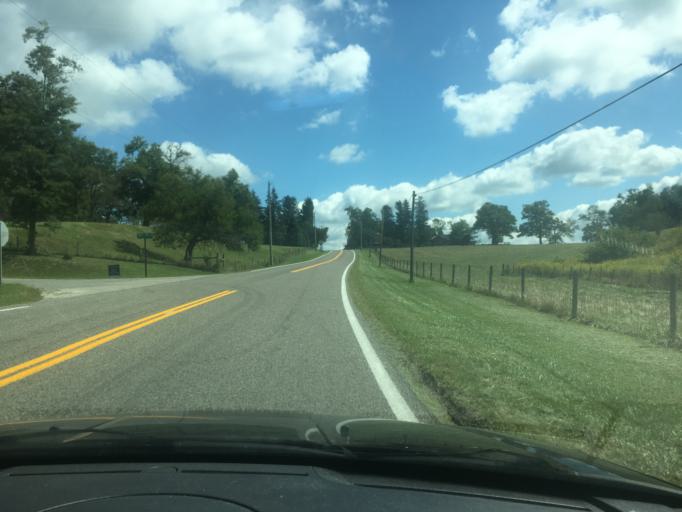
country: US
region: Ohio
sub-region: Logan County
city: West Liberty
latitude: 40.2342
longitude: -83.7219
